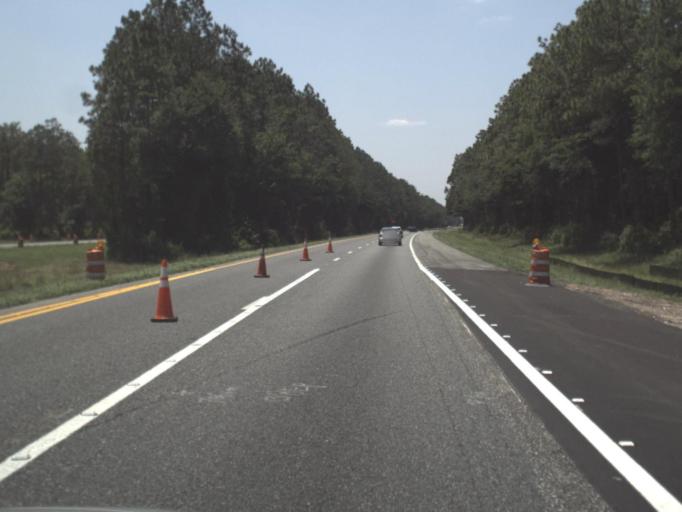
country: US
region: Florida
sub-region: Columbia County
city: Watertown
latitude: 30.2427
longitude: -82.5775
